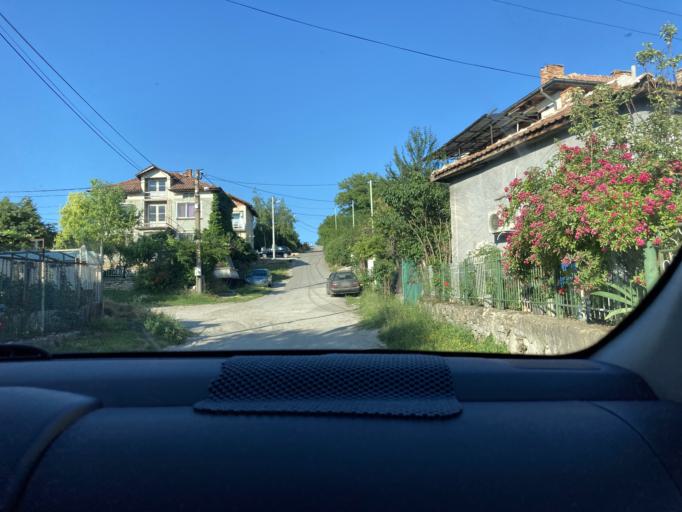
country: BG
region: Sofiya
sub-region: Obshtina Slivnitsa
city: Slivnitsa
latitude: 42.8486
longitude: 22.9902
